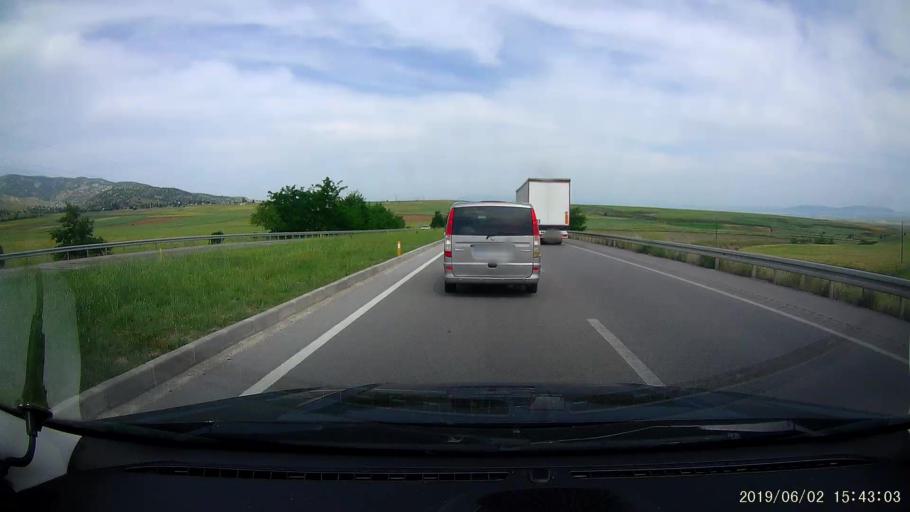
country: TR
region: Amasya
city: Alicik
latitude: 40.8675
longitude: 35.3274
